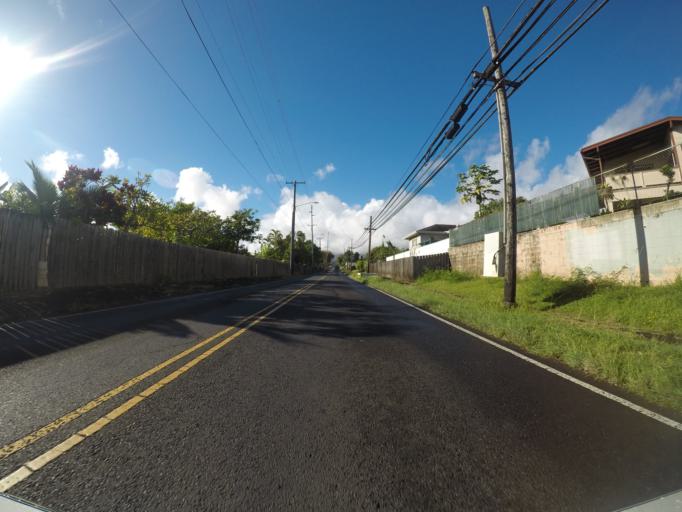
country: US
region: Hawaii
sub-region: Honolulu County
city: He'eia
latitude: 21.4248
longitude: -157.8059
